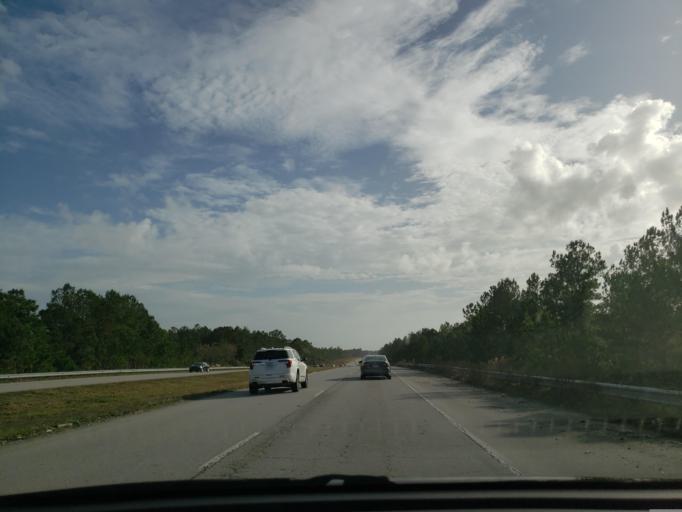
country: US
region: North Carolina
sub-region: Onslow County
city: Sneads Ferry
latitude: 34.6137
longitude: -77.4841
